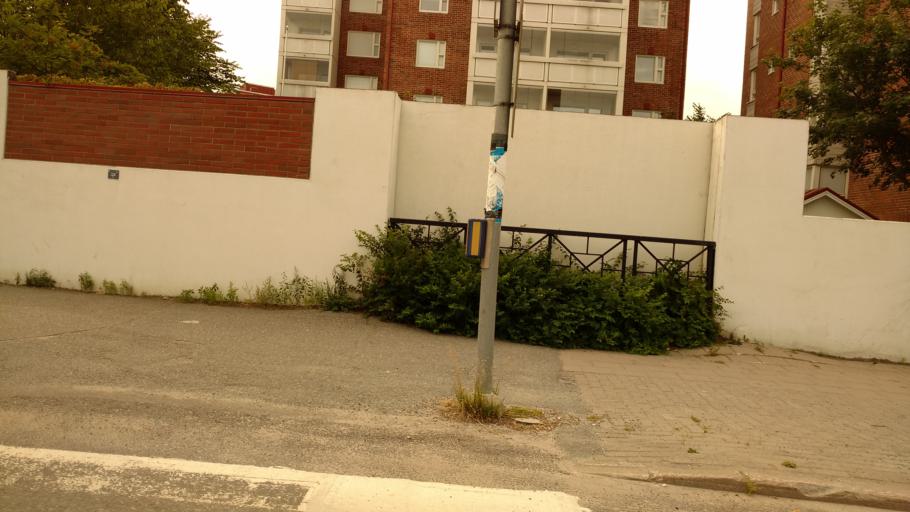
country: FI
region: Varsinais-Suomi
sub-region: Turku
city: Turku
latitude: 60.4587
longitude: 22.2740
